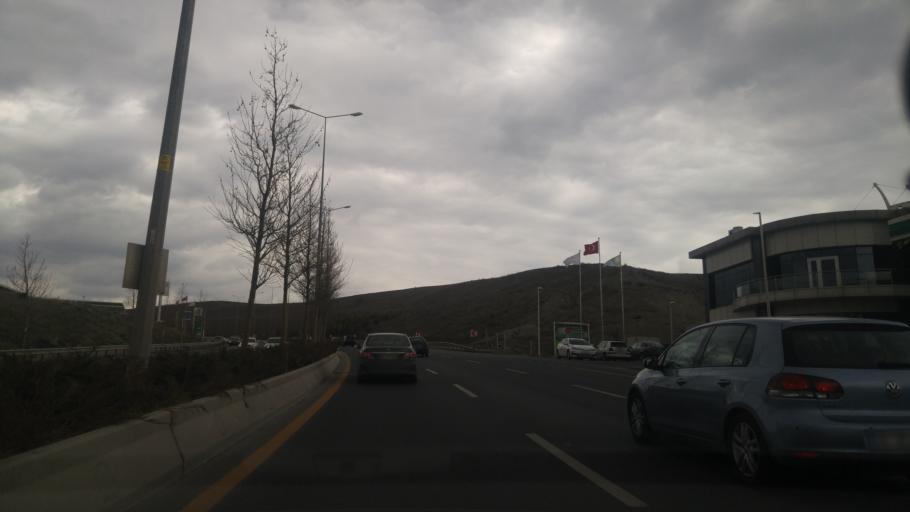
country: TR
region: Ankara
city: Mamak
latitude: 39.8847
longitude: 32.9186
